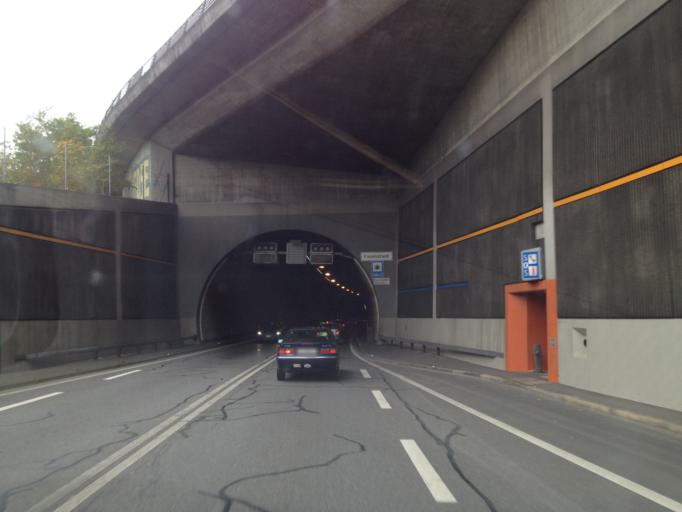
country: CH
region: Schaffhausen
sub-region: Bezirk Schaffhausen
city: Schaffhausen
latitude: 47.7049
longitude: 8.6365
